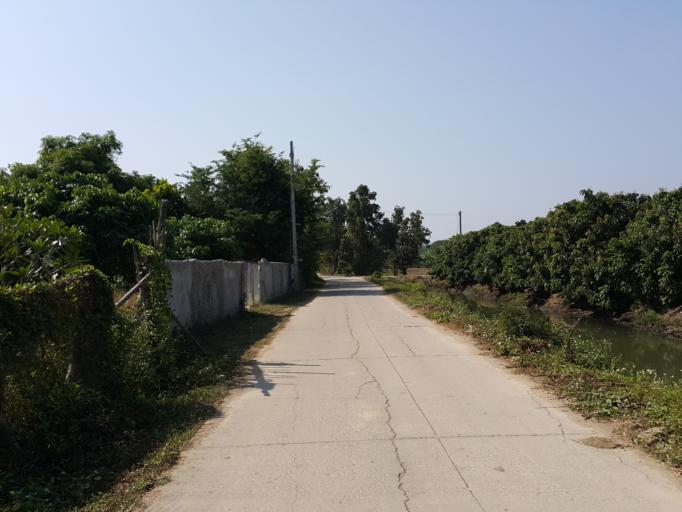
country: TH
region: Lamphun
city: Lamphun
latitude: 18.5991
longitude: 98.9898
